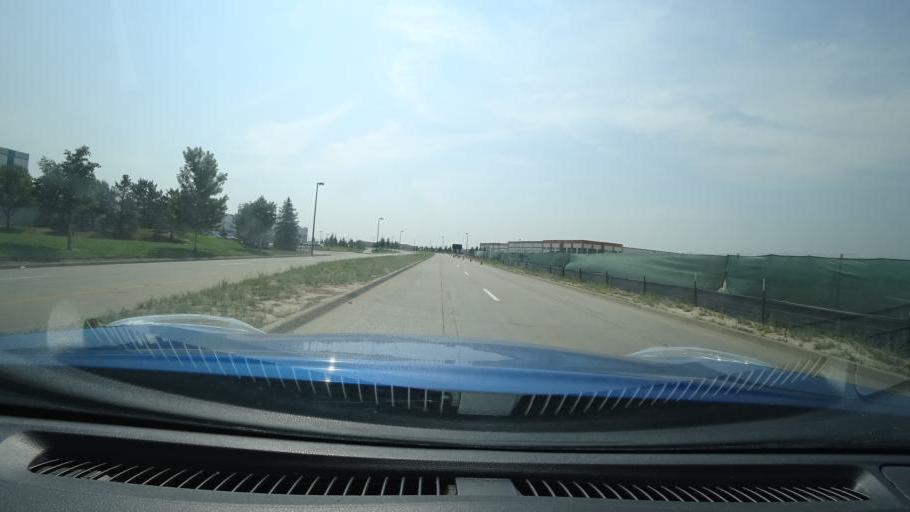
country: US
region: Colorado
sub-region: Adams County
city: Aurora
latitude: 39.7709
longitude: -104.7774
